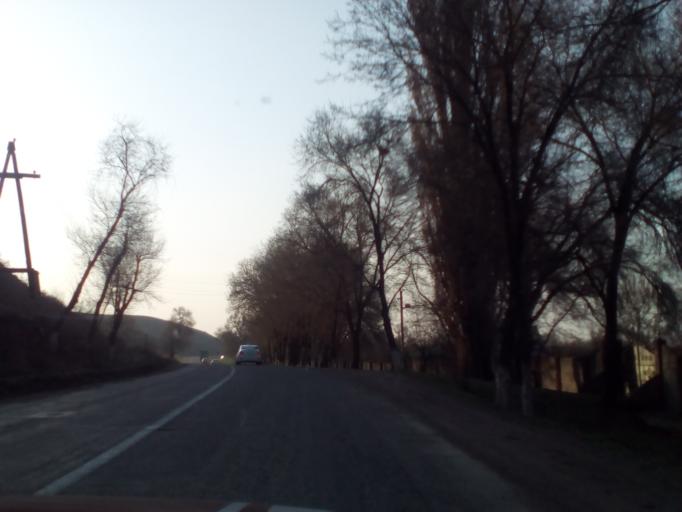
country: KZ
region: Almaty Oblysy
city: Burunday
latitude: 43.1690
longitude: 76.5393
